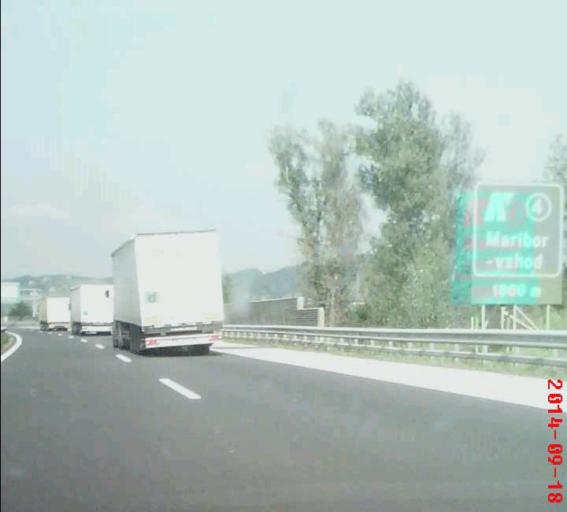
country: SI
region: Miklavz na Dravskem Polju
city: Miklavz na Dravskem Polju
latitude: 46.5251
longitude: 15.6949
